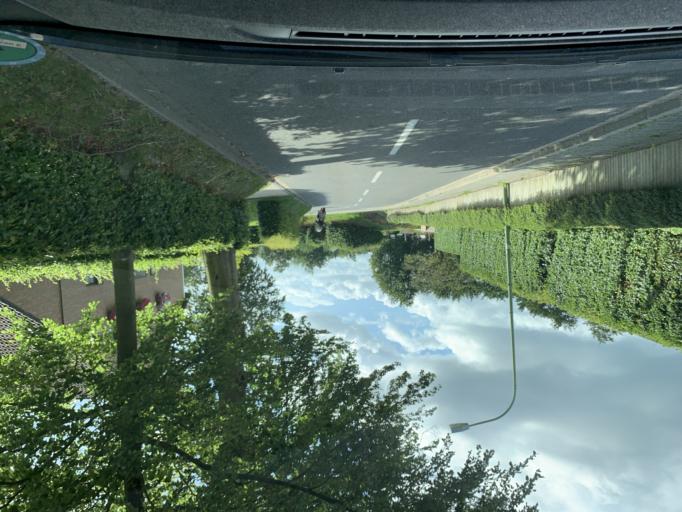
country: DE
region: North Rhine-Westphalia
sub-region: Regierungsbezirk Koln
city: Monschau
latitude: 50.5911
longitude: 6.2548
